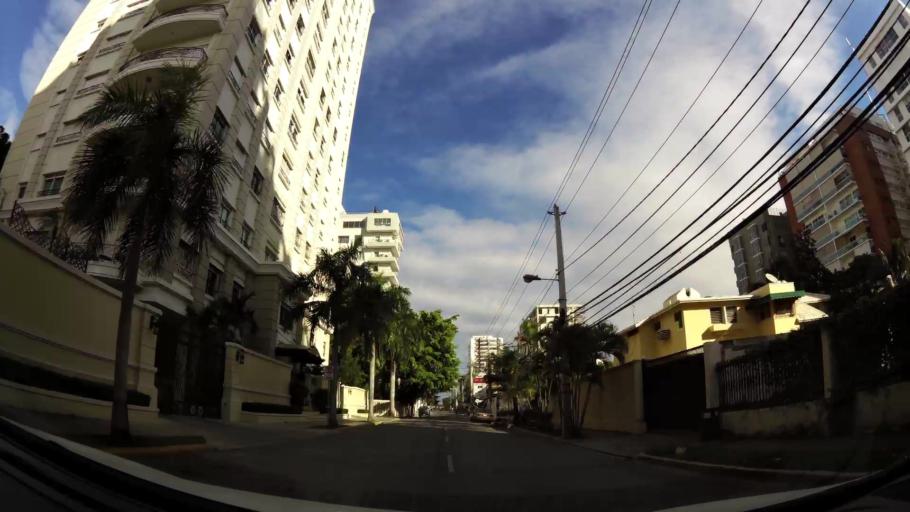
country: DO
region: Nacional
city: La Julia
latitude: 18.4784
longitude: -69.9400
